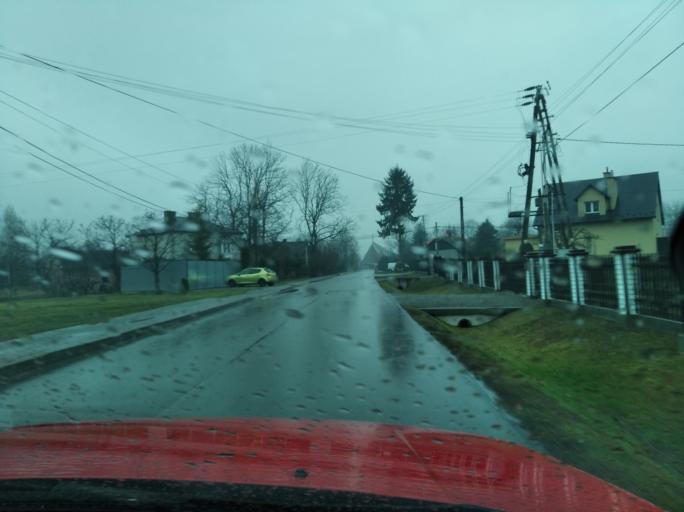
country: PL
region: Subcarpathian Voivodeship
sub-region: Powiat lancucki
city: Krzemienica
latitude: 50.0796
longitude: 22.1391
